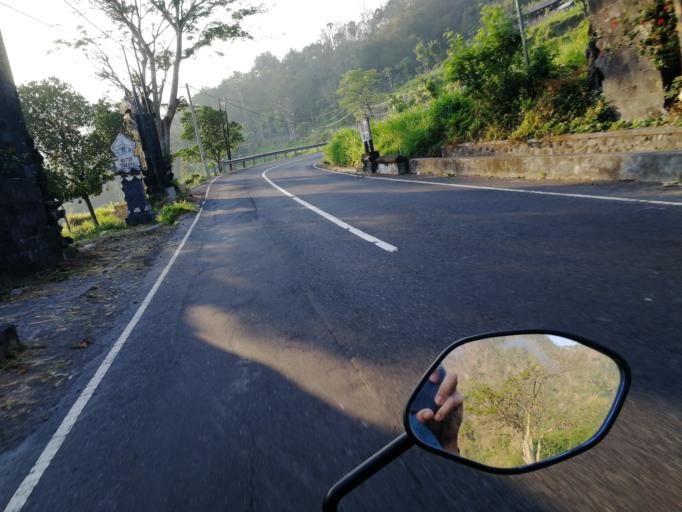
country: ID
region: Bali
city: Banjar Kangkaang
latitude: -8.3660
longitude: 115.6118
